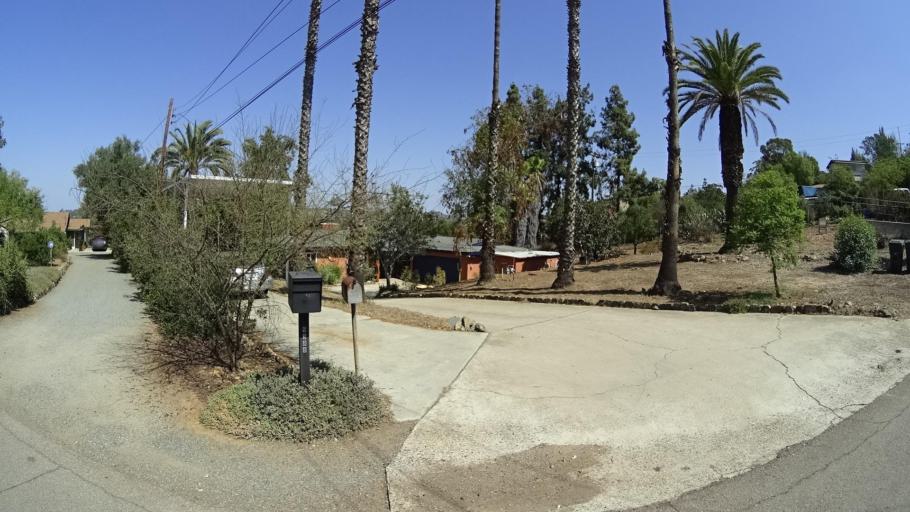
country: US
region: California
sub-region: San Diego County
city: Spring Valley
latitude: 32.7356
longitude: -116.9961
